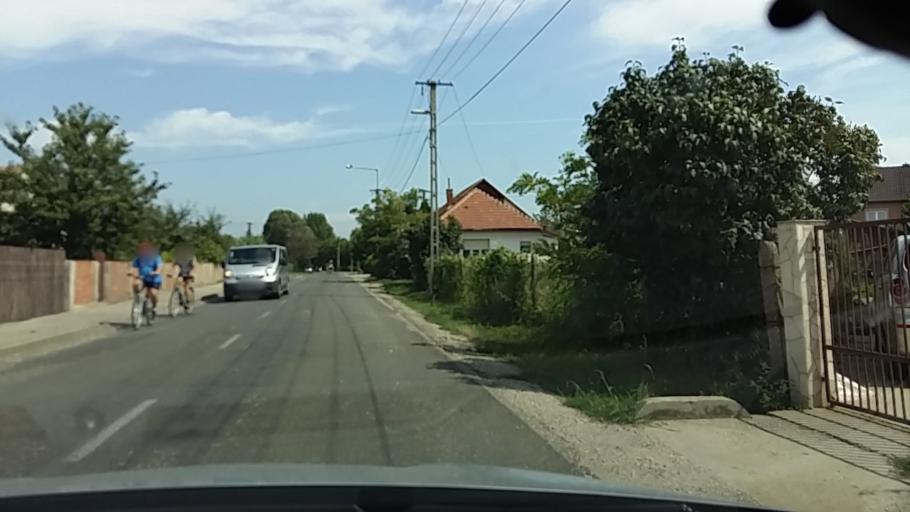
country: HU
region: Borsod-Abauj-Zemplen
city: Malyi
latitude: 48.0647
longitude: 20.8278
